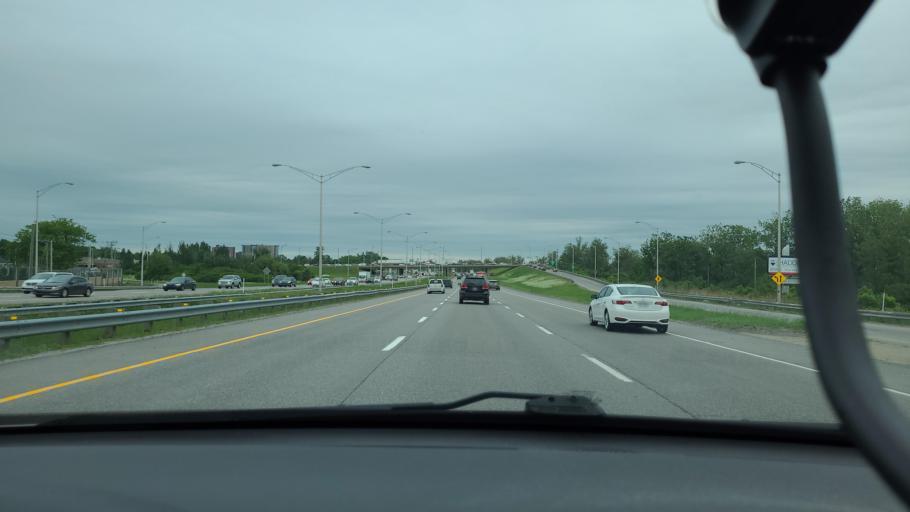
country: CA
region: Quebec
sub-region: Laval
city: Laval
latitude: 45.5906
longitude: -73.7221
